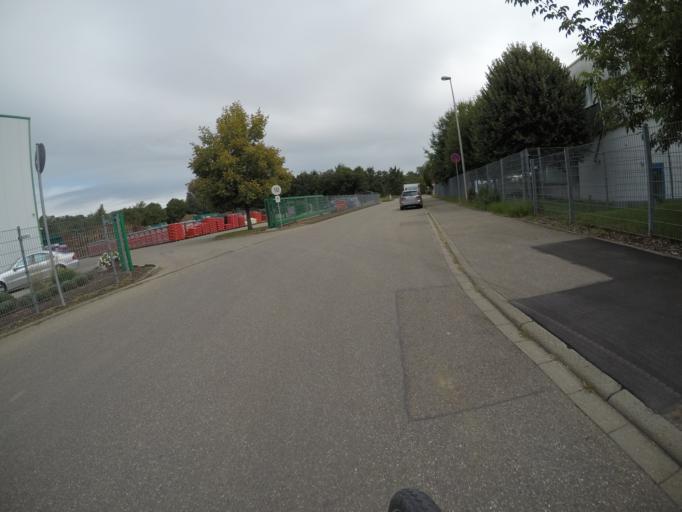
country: DE
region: Baden-Wuerttemberg
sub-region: Regierungsbezirk Stuttgart
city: Marbach am Neckar
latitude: 48.8936
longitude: 9.2603
